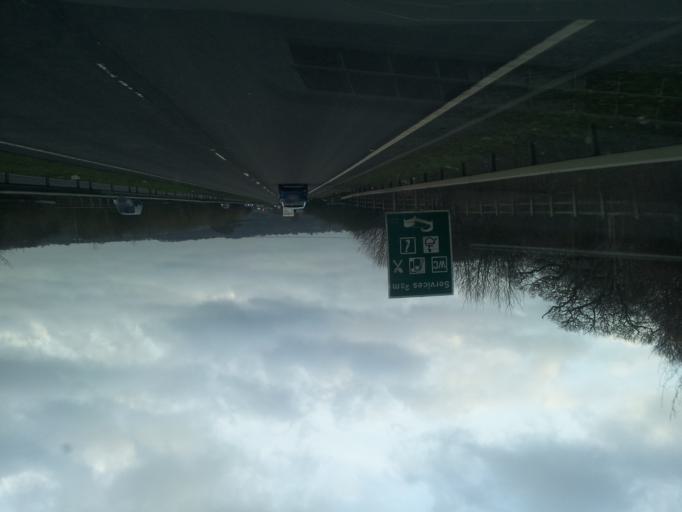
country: GB
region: England
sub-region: Hertfordshire
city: Berkhamsted
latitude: 51.7472
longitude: -0.5482
